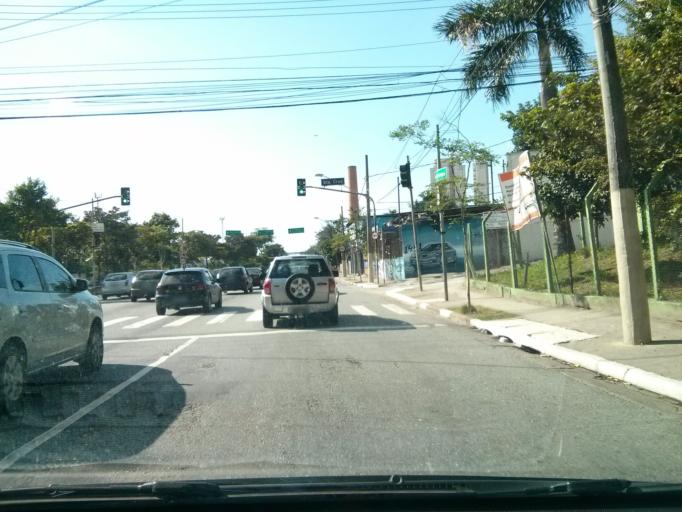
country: BR
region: Sao Paulo
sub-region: Sao Paulo
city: Sao Paulo
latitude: -23.5998
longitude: -46.6236
